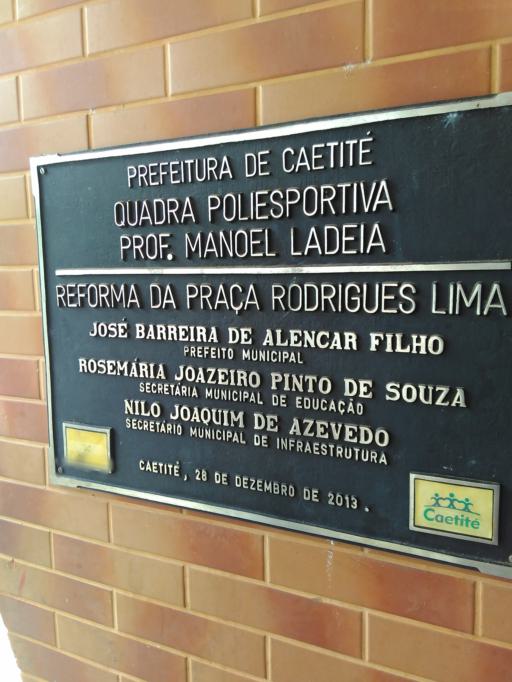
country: BR
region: Bahia
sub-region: Caetite
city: Caetite
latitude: -14.0710
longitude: -42.4845
